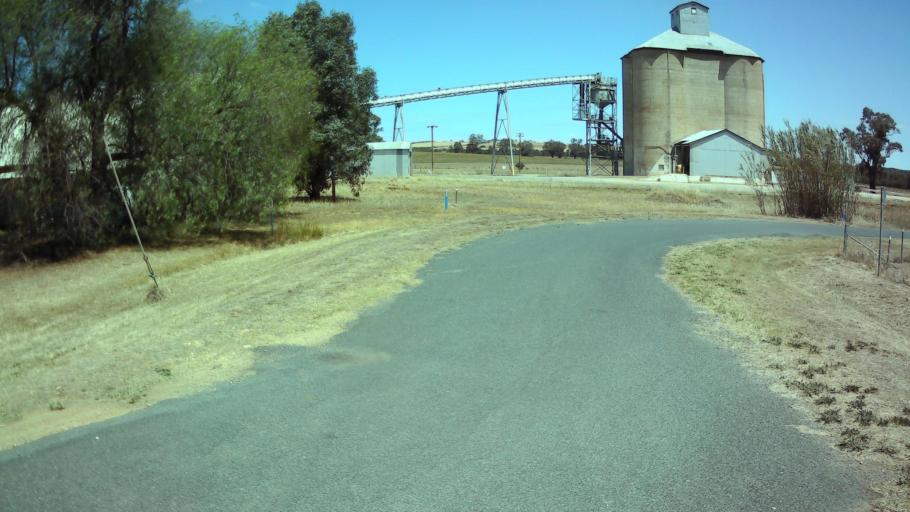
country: AU
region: New South Wales
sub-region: Weddin
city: Grenfell
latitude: -33.9967
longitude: 148.4043
